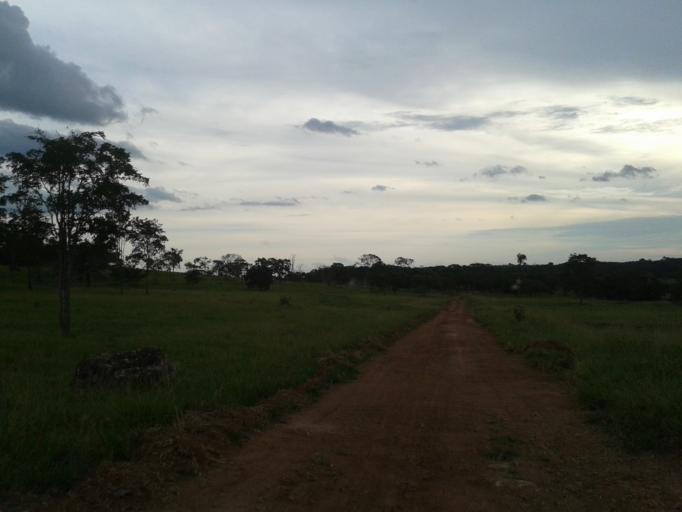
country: BR
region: Minas Gerais
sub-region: Campina Verde
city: Campina Verde
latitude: -19.4126
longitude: -49.5941
